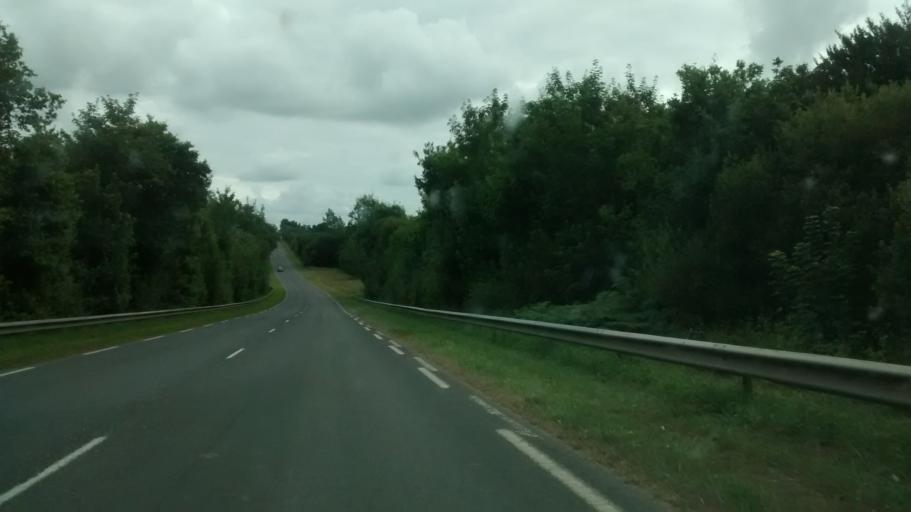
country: FR
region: Brittany
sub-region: Departement du Finistere
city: Le Folgoet
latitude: 48.5519
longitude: -4.3466
